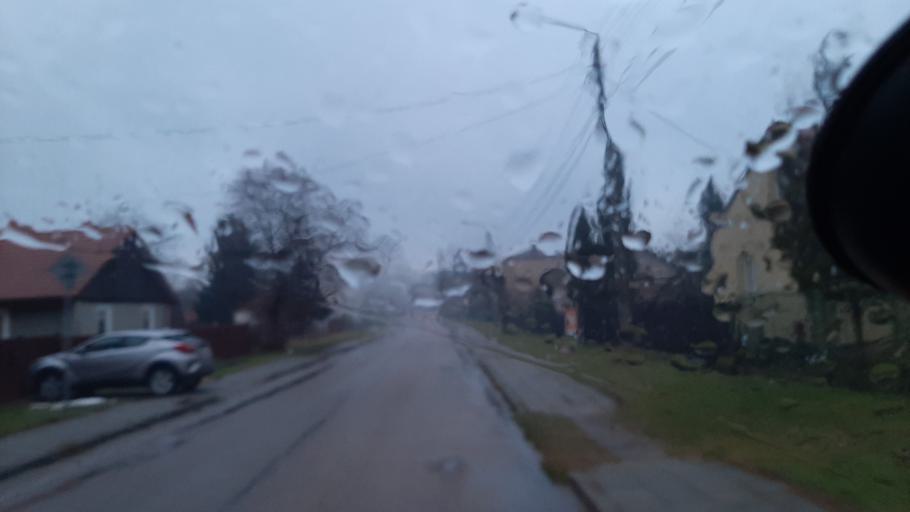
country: PL
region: Lublin Voivodeship
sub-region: Powiat lubartowski
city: Firlej
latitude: 51.5571
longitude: 22.5085
